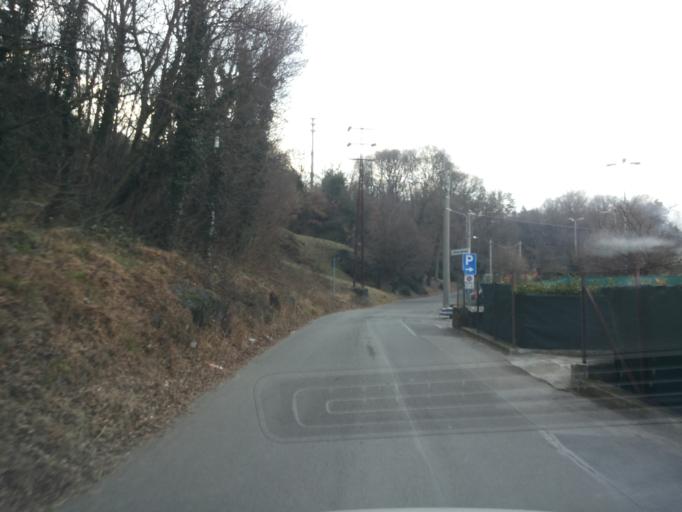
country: IT
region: Piedmont
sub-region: Provincia di Torino
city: Ivrea
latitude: 45.4563
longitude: 7.8732
